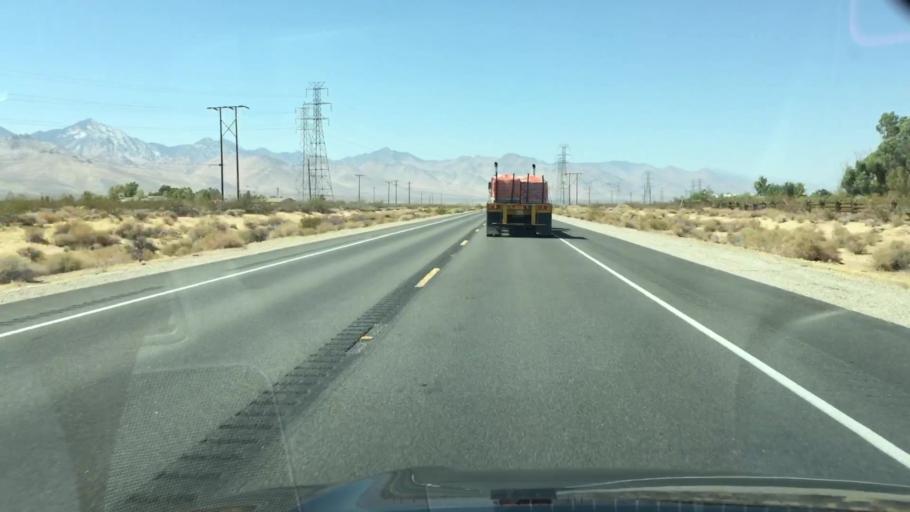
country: US
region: California
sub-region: Kern County
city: Inyokern
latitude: 35.6382
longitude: -117.7892
